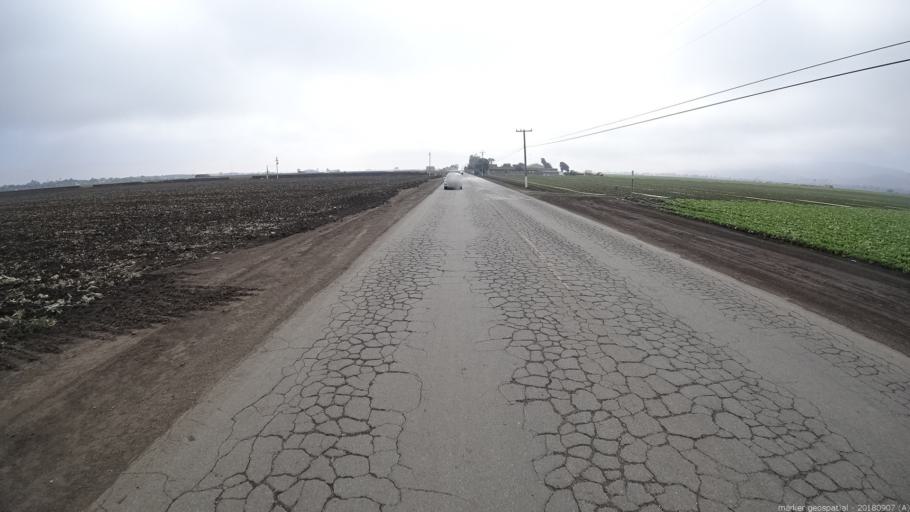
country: US
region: California
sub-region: Monterey County
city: Salinas
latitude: 36.6525
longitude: -121.6797
